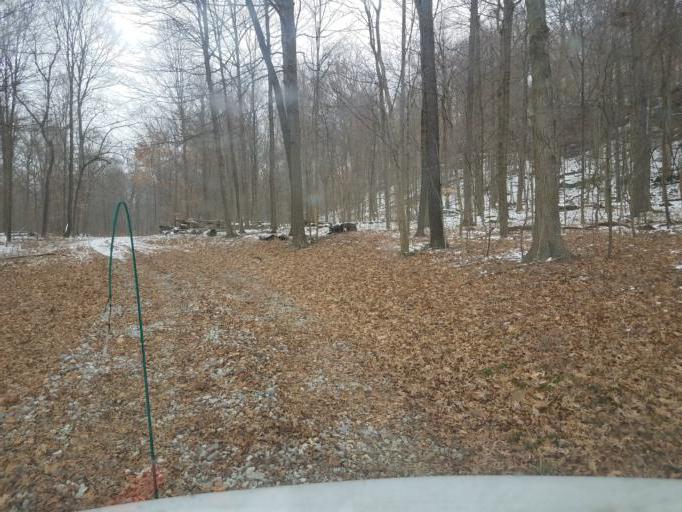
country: US
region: Ohio
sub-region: Sandusky County
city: Bellville
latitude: 40.6605
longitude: -82.4105
